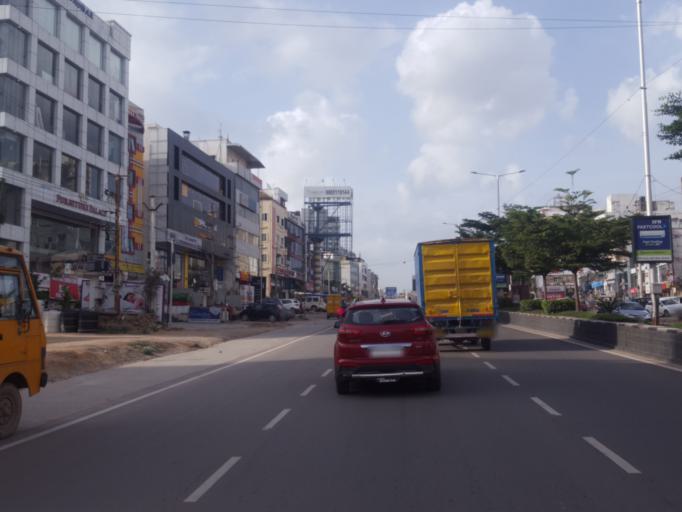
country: IN
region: Telangana
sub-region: Rangareddi
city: Kukatpalli
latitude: 17.4437
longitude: 78.3628
